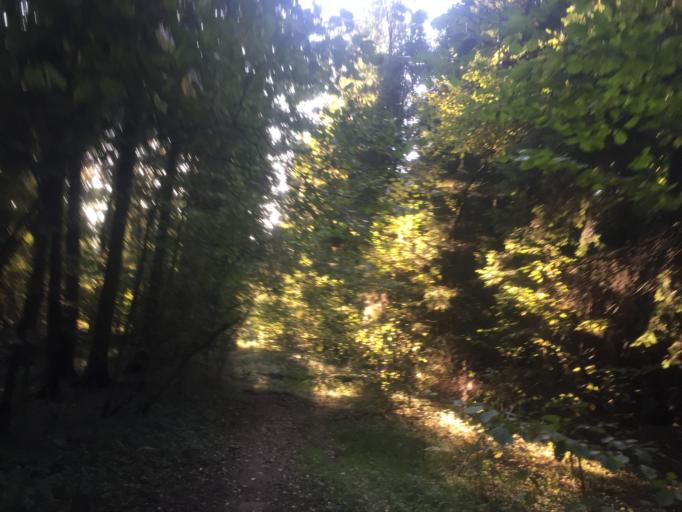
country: RU
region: Moscow
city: Gol'yanovo
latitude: 55.8439
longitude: 37.7933
